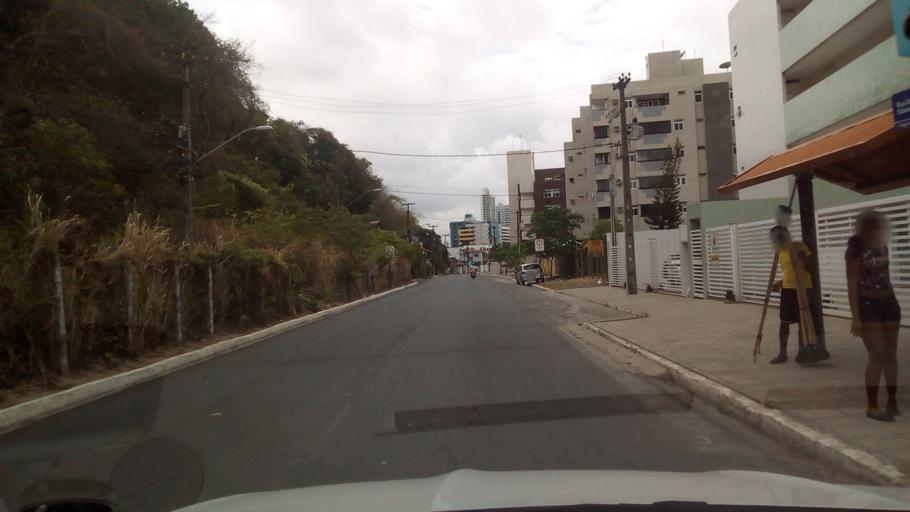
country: BR
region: Paraiba
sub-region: Joao Pessoa
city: Joao Pessoa
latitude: -7.1302
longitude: -34.8246
